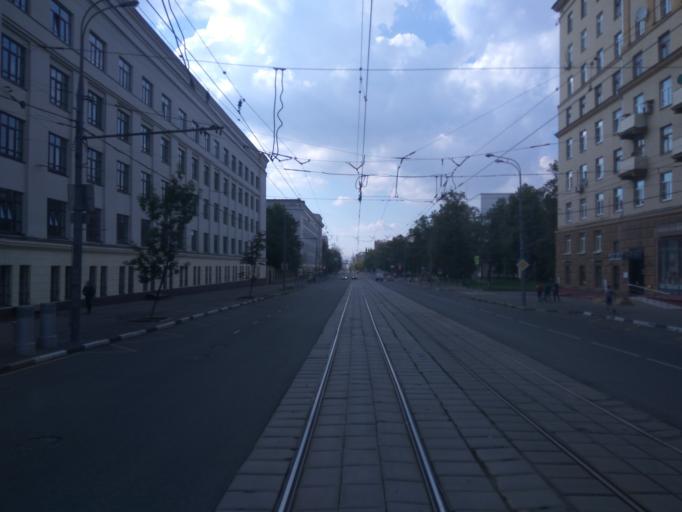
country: RU
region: Moscow
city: Lefortovo
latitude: 55.7537
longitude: 37.7103
